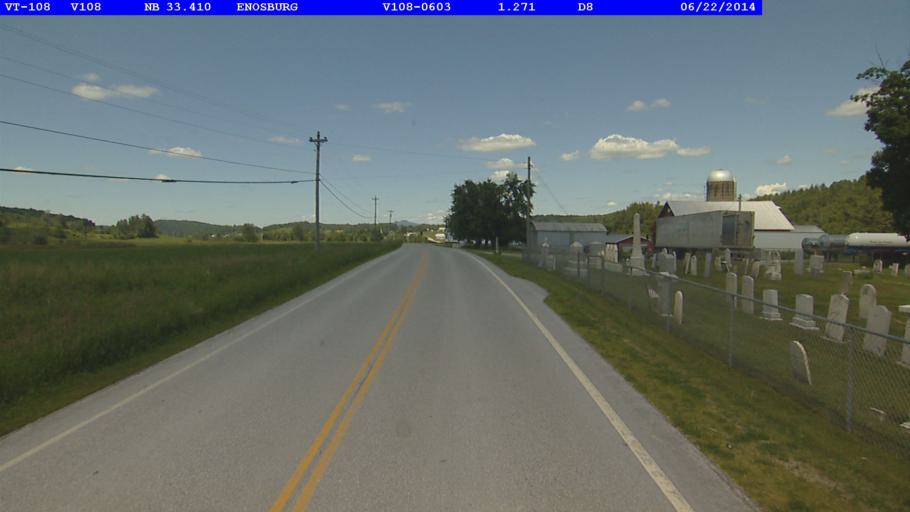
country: US
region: Vermont
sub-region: Franklin County
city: Enosburg Falls
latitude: 44.8561
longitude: -72.8023
